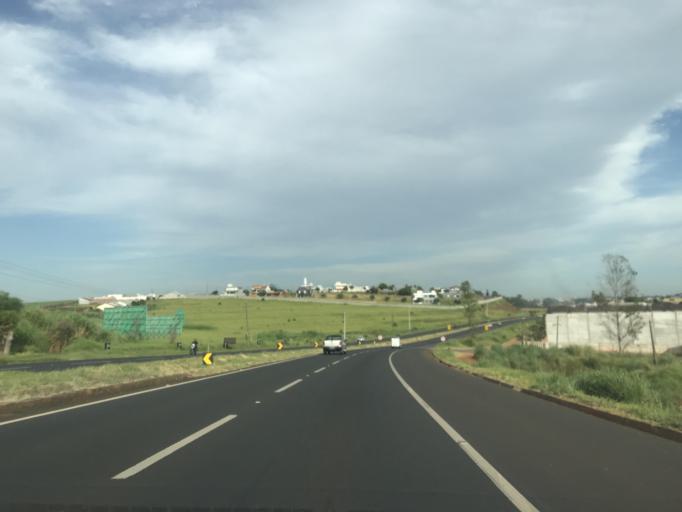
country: BR
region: Parana
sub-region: Mandaguacu
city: Mandaguacu
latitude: -23.3654
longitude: -52.0815
